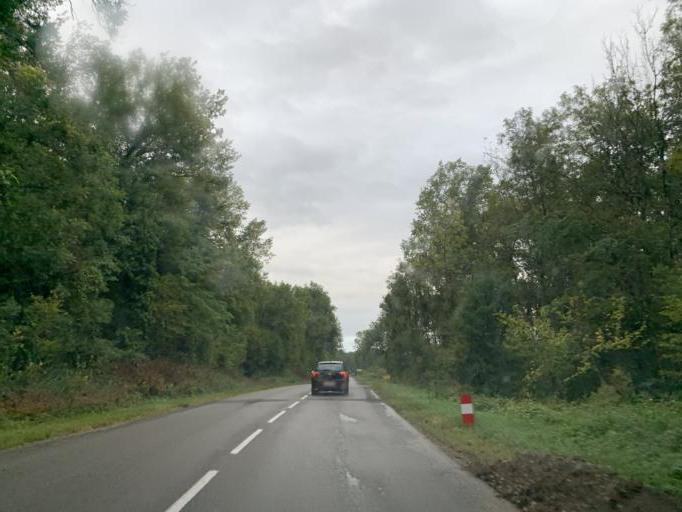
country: FR
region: Rhone-Alpes
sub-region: Departement de l'Isere
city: Les Avenieres
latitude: 45.6804
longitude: 5.6034
